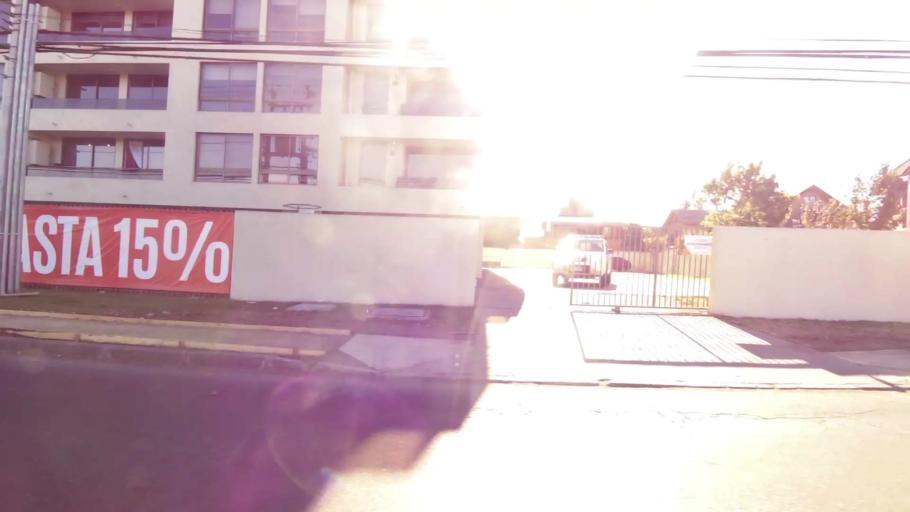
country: CL
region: Biobio
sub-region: Provincia de Concepcion
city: Concepcion
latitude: -36.8367
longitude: -73.1018
